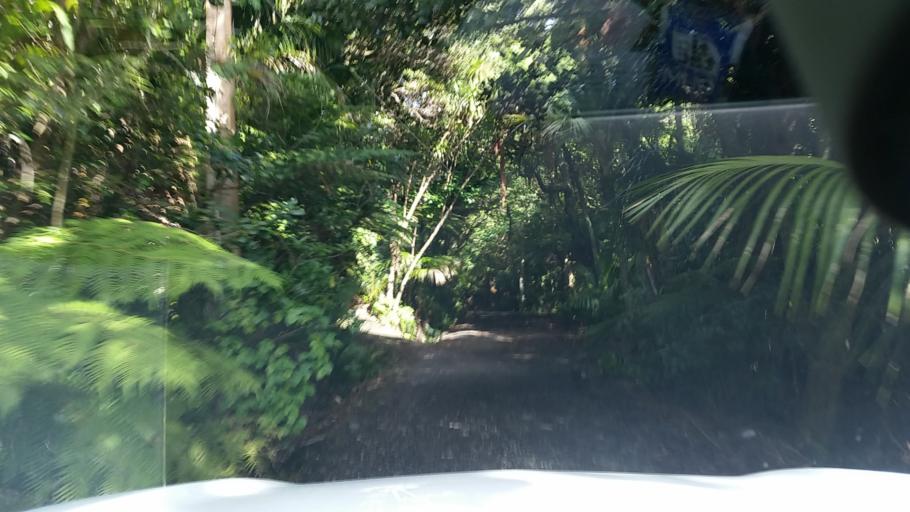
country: NZ
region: Auckland
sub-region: Auckland
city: Titirangi
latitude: -36.9937
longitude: 174.4855
